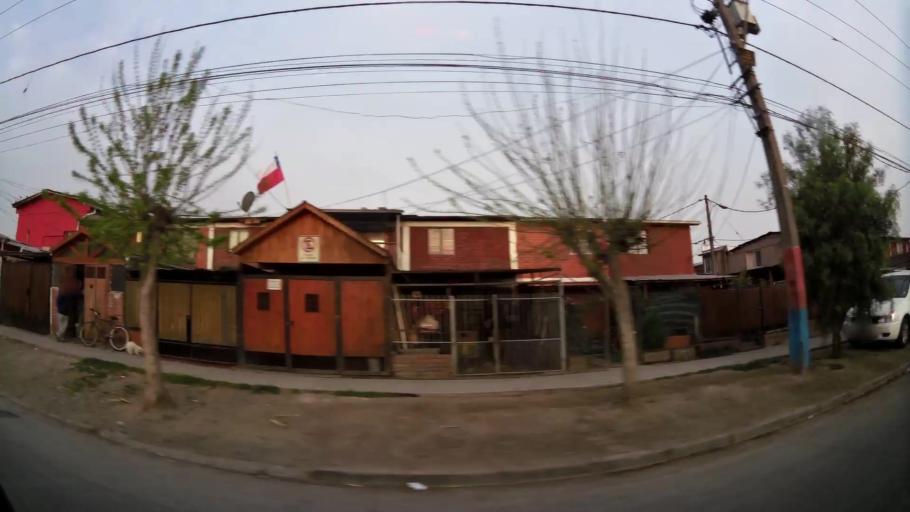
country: CL
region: Santiago Metropolitan
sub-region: Provincia de Santiago
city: Lo Prado
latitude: -33.5141
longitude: -70.7851
